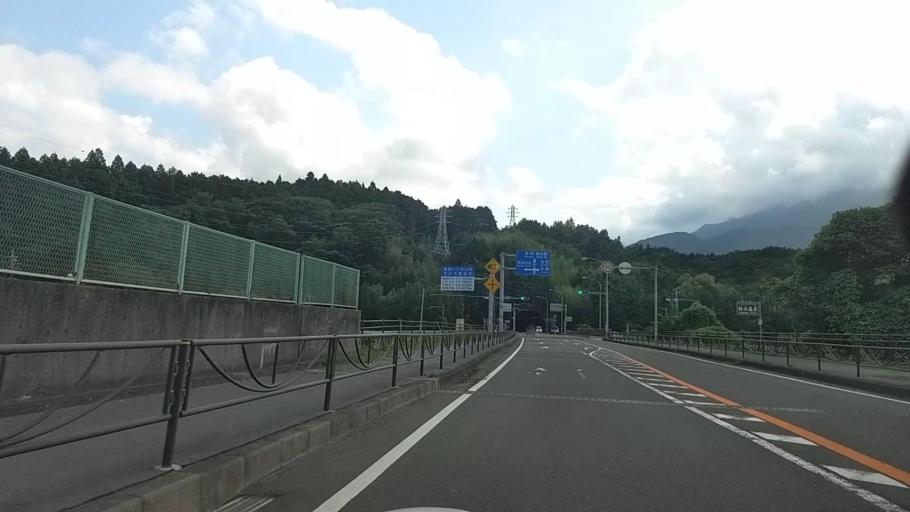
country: JP
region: Shizuoka
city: Fujinomiya
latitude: 35.2962
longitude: 138.4471
